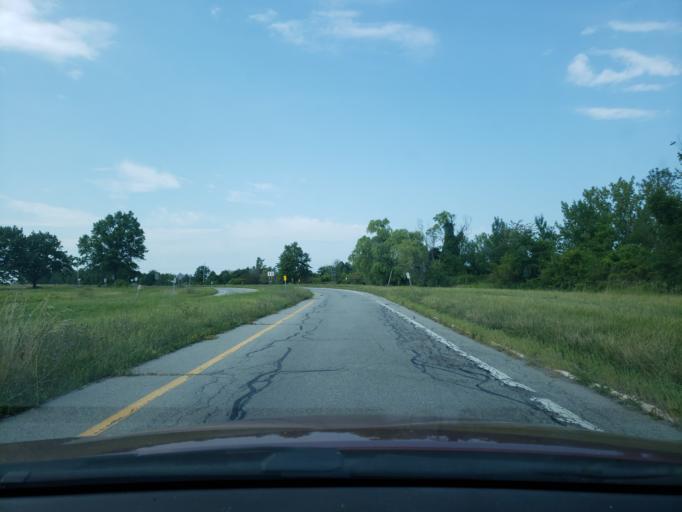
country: US
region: New York
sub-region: Monroe County
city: Greece
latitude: 43.2804
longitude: -77.6935
